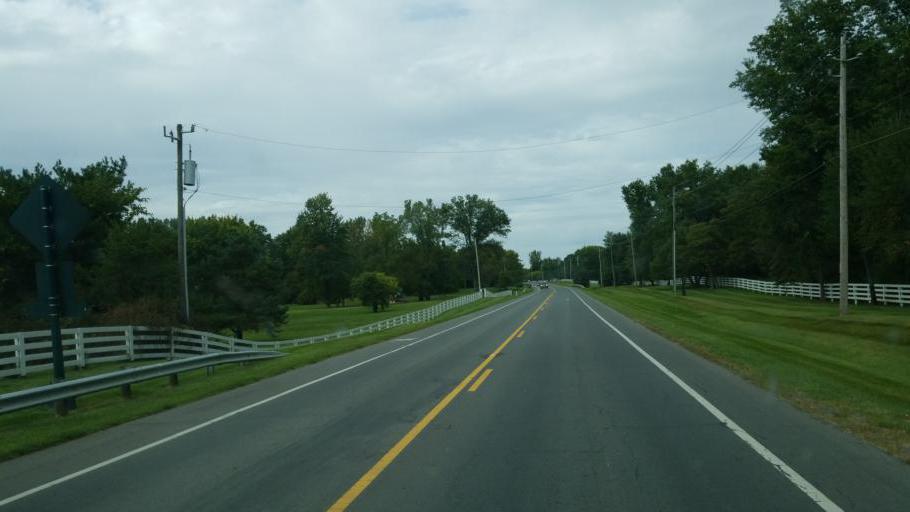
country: US
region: Ohio
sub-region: Franklin County
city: New Albany
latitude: 40.0549
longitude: -82.8104
